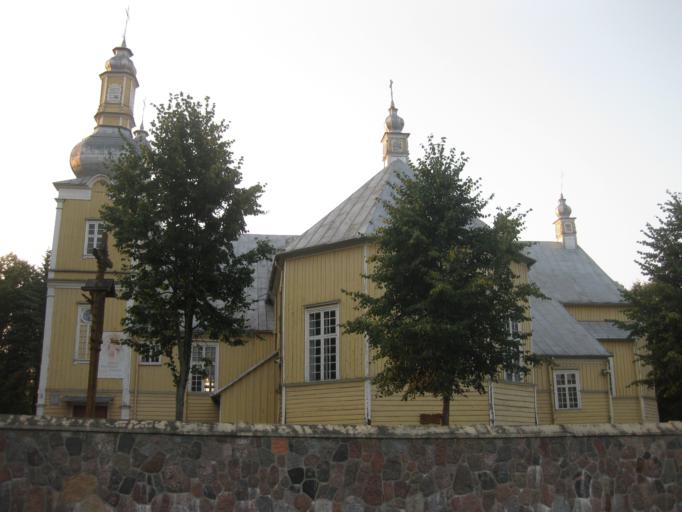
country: LT
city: Prienai
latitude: 54.6347
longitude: 23.9497
